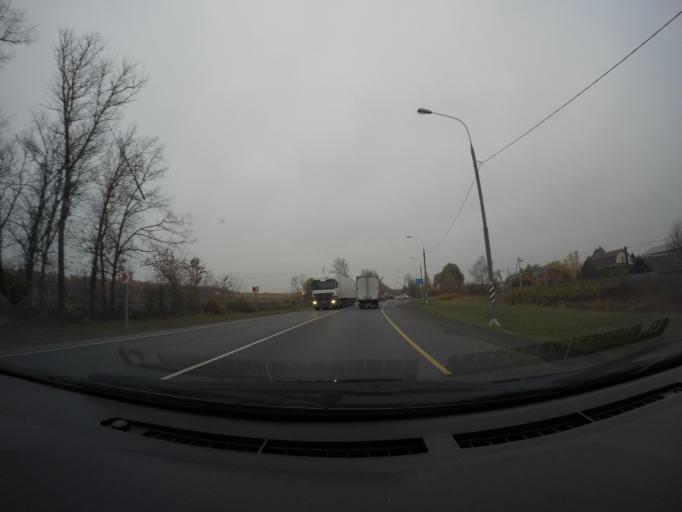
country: RU
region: Moskovskaya
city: Bronnitsy
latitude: 55.3835
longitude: 38.1887
